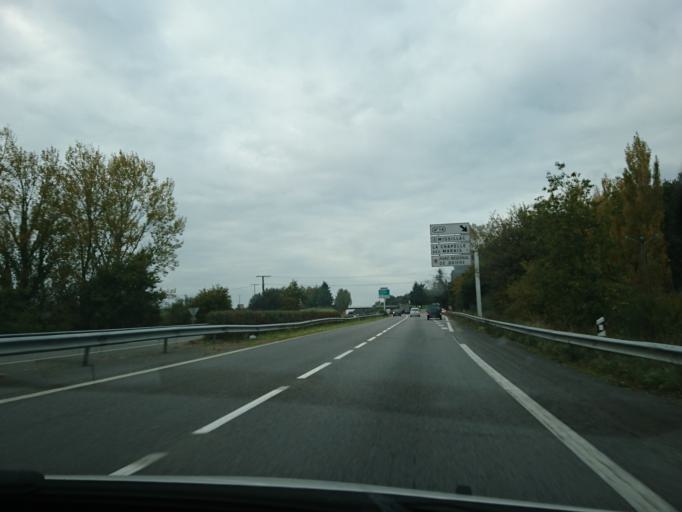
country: FR
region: Pays de la Loire
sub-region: Departement de la Loire-Atlantique
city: Missillac
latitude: 47.4748
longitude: -2.1776
